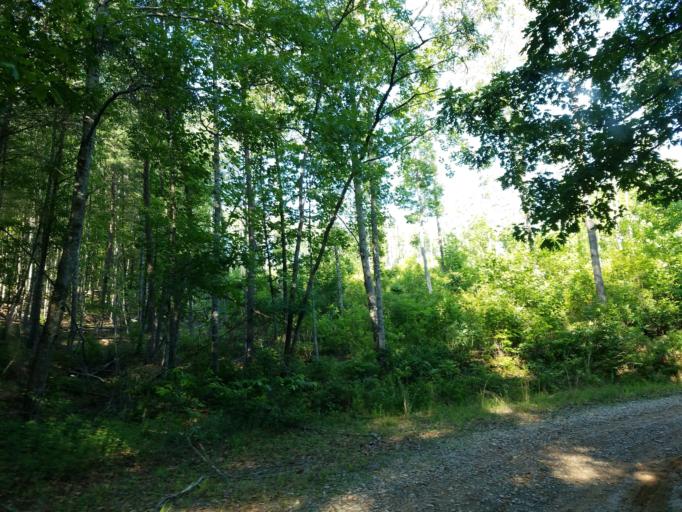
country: US
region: Georgia
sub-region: Fannin County
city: Blue Ridge
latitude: 34.7985
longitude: -84.1924
